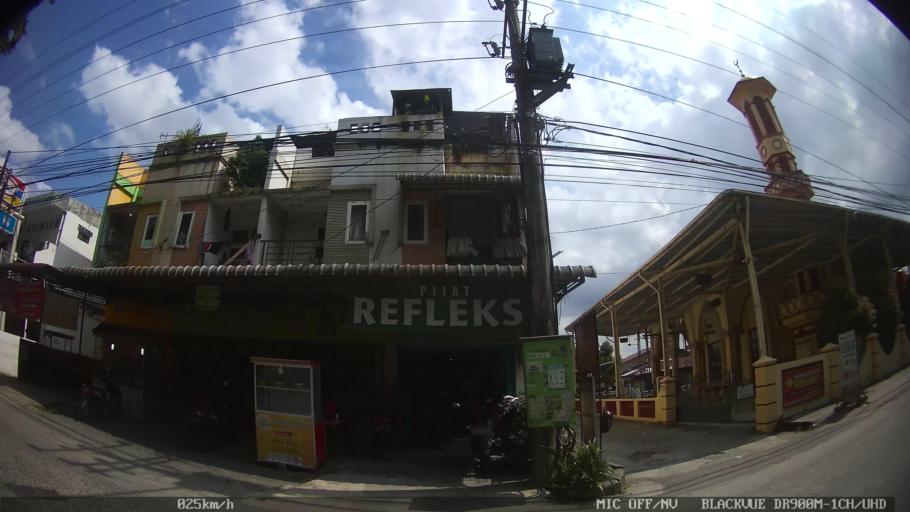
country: ID
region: North Sumatra
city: Sunggal
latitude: 3.6047
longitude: 98.6371
